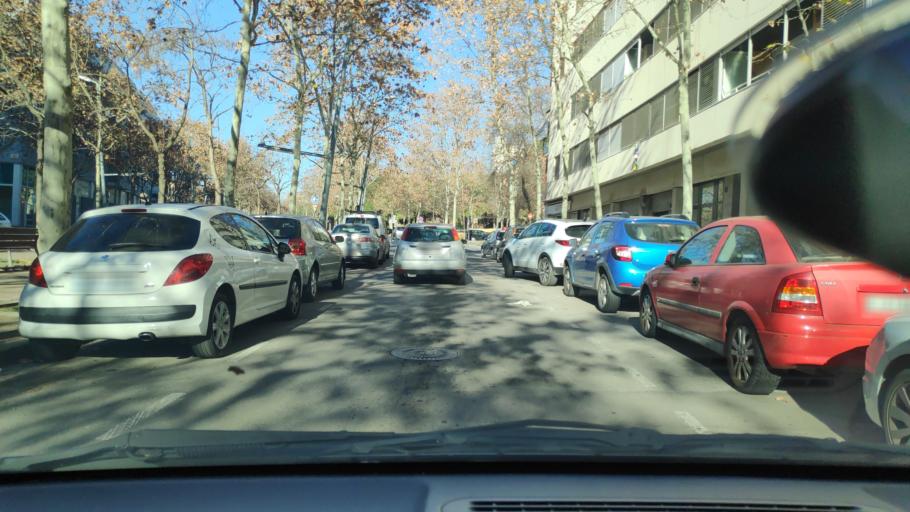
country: ES
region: Catalonia
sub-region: Provincia de Barcelona
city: Sant Quirze del Valles
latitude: 41.5481
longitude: 2.0897
